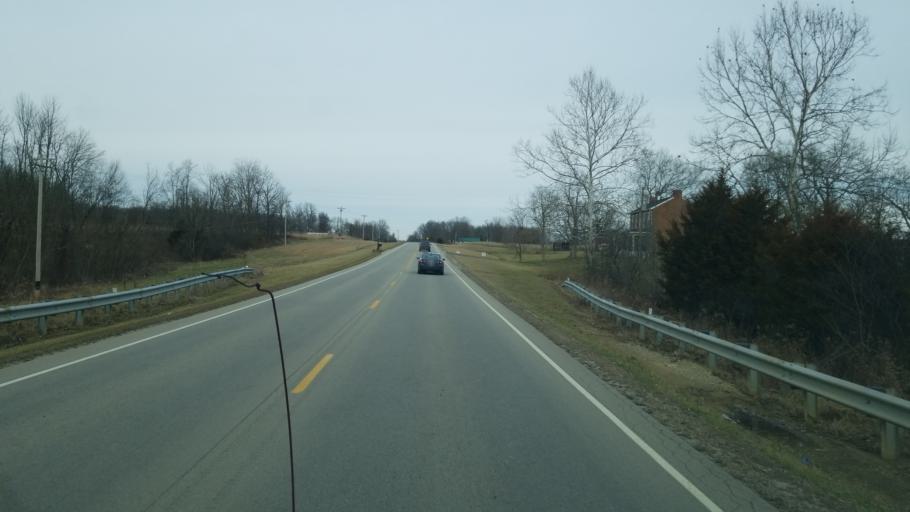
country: US
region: Ohio
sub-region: Highland County
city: Hillsboro
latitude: 39.0818
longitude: -83.6843
